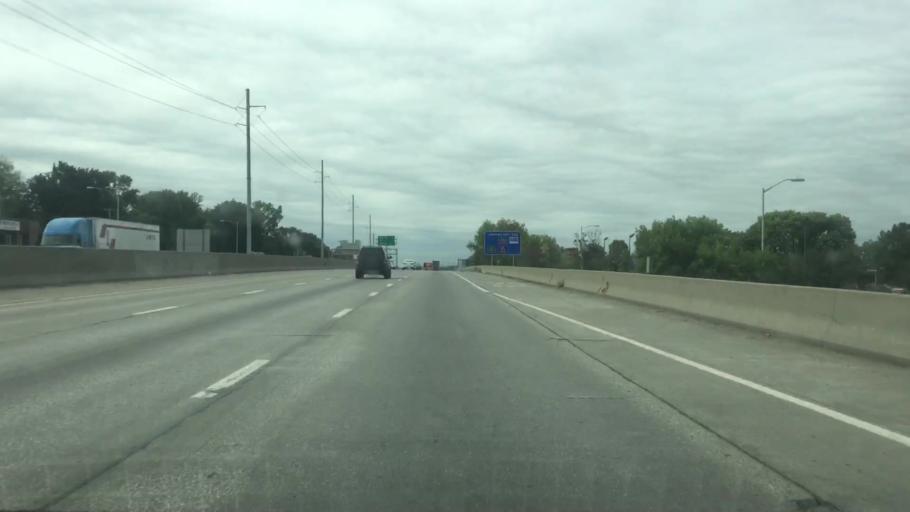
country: US
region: Kansas
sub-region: Johnson County
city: Lenexa
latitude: 38.9655
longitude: -94.7245
